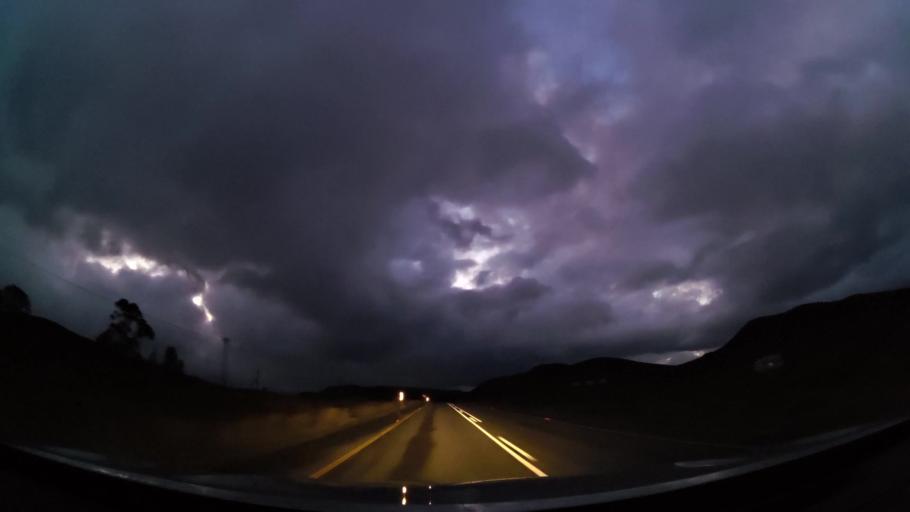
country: ZA
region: Western Cape
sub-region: Overberg District Municipality
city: Swellendam
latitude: -33.9000
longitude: 20.3889
